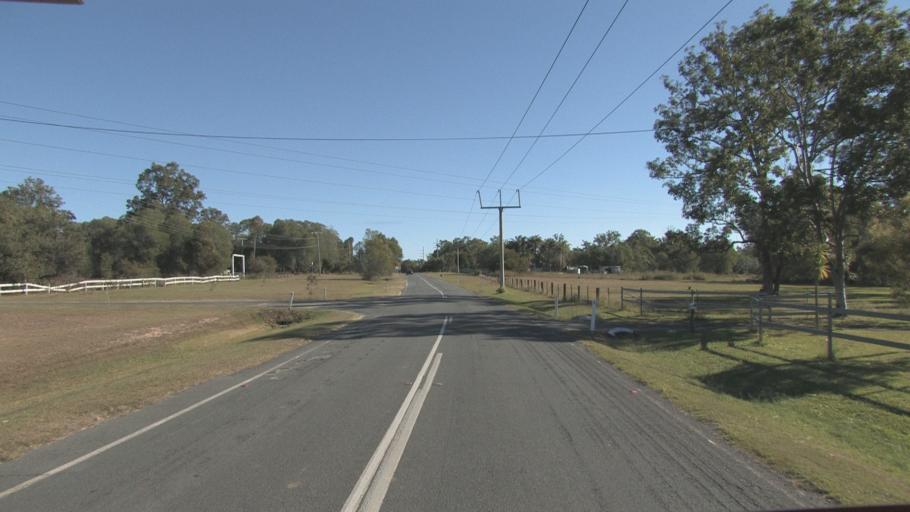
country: AU
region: Queensland
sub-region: Logan
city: Chambers Flat
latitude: -27.7820
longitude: 153.0558
